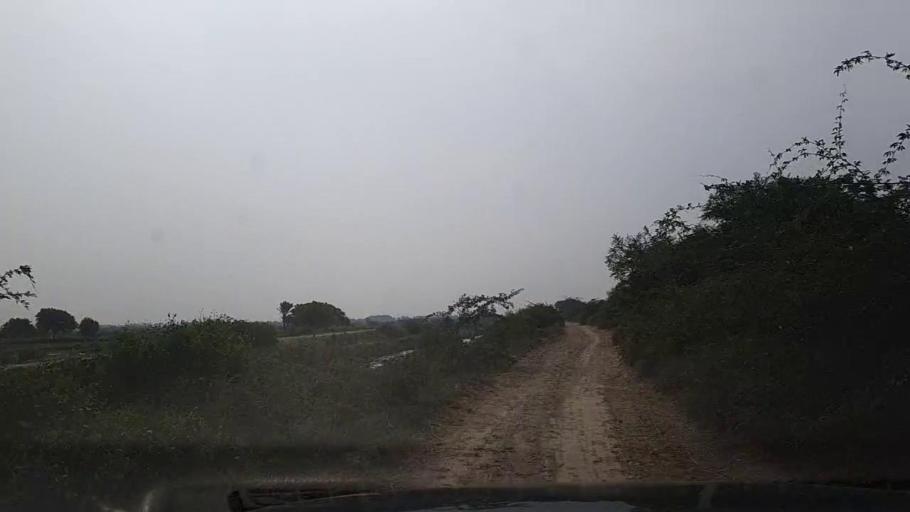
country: PK
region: Sindh
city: Thatta
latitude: 24.7518
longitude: 67.8082
